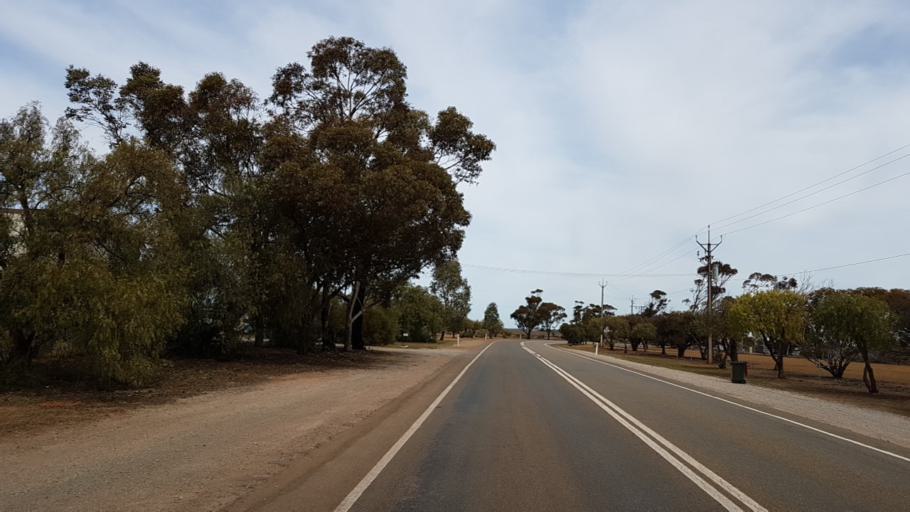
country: AU
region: South Australia
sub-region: Peterborough
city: Peterborough
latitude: -32.9771
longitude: 138.8200
